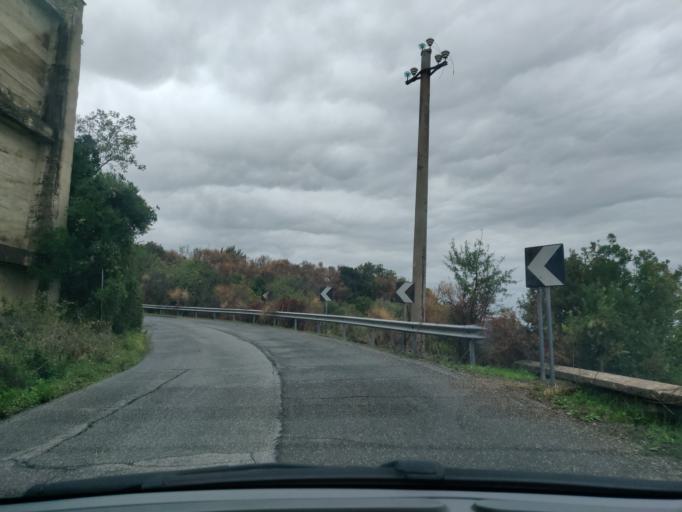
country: IT
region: Latium
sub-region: Citta metropolitana di Roma Capitale
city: Allumiere
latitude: 42.1263
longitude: 11.8554
